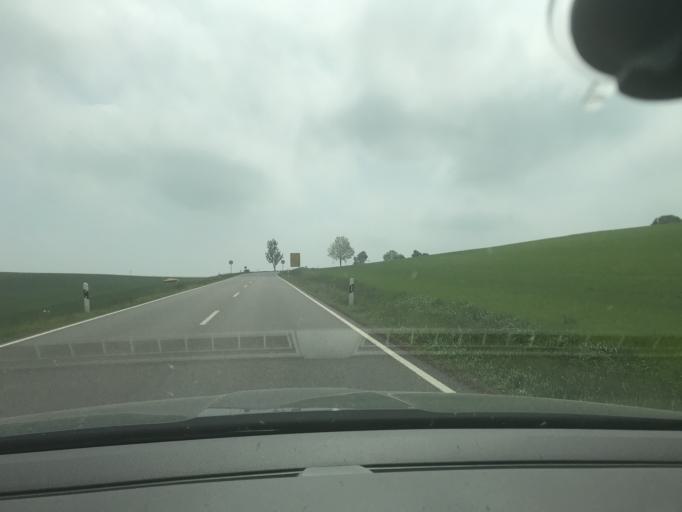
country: DE
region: Saxony
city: Grosshartmannsdorf
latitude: 50.7808
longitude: 13.3220
